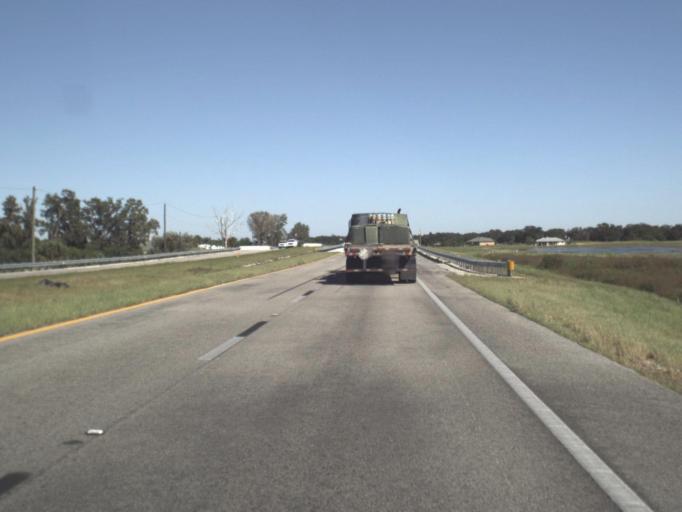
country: US
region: Florida
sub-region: Hendry County
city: Port LaBelle
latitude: 26.7626
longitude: -81.4023
